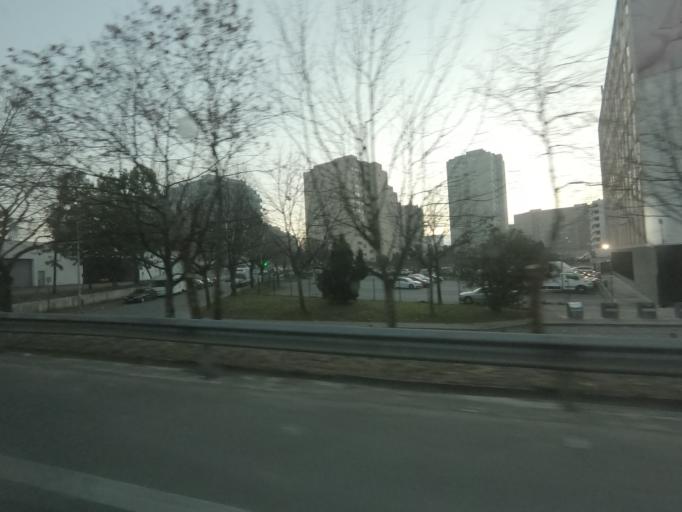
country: PT
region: Porto
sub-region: Matosinhos
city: Senhora da Hora
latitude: 41.1794
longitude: -8.6235
